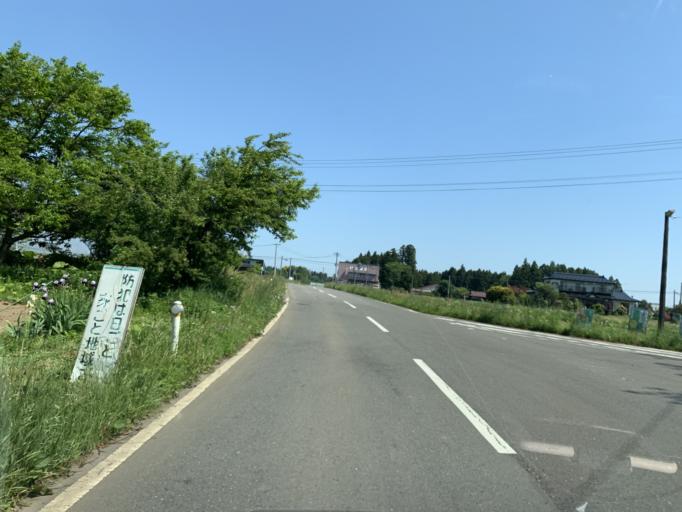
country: JP
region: Iwate
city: Mizusawa
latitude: 39.0969
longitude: 141.0757
